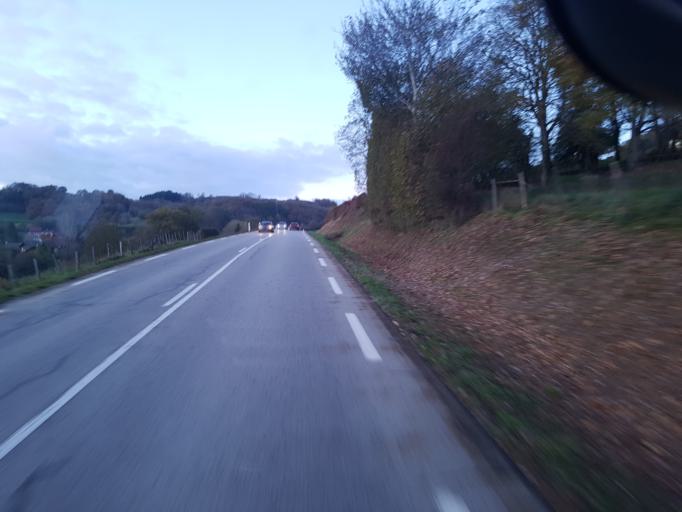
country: FR
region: Rhone-Alpes
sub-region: Departement de l'Isere
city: Bilieu
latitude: 45.4429
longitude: 5.5649
